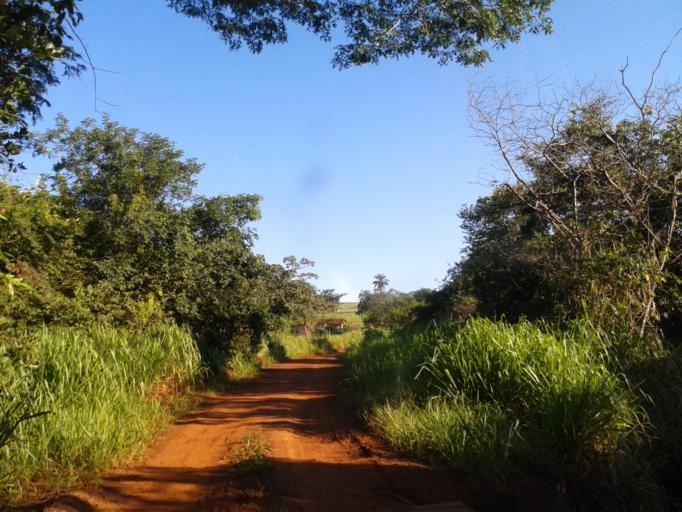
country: BR
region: Minas Gerais
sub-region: Centralina
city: Centralina
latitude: -18.6858
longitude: -49.2834
